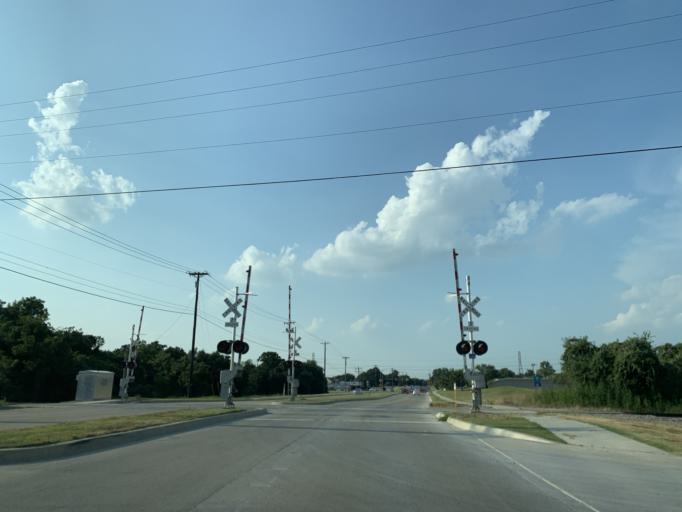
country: US
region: Texas
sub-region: Tarrant County
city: Hurst
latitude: 32.8065
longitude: -97.1866
